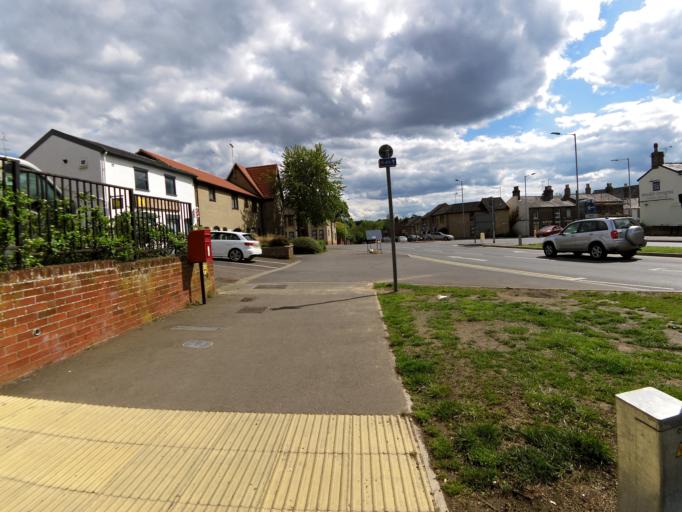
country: GB
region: England
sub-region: Suffolk
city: Bury St Edmunds
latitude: 52.2414
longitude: 0.7117
